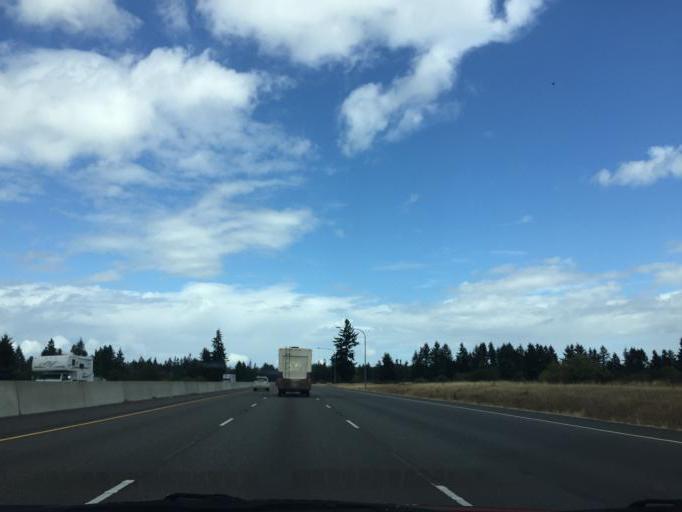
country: US
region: Washington
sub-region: Thurston County
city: Grand Mound
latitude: 46.8431
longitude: -122.9828
